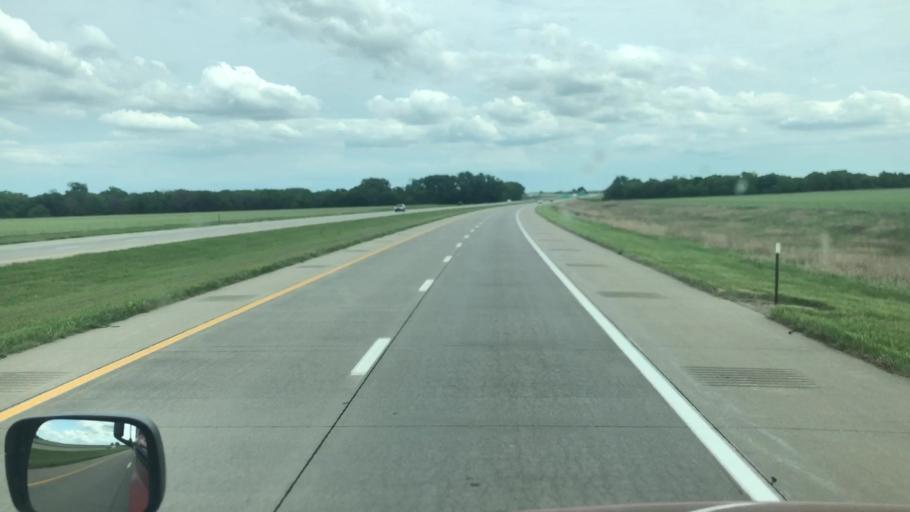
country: US
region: Kansas
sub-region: McPherson County
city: Moundridge
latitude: 38.2445
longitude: -97.5344
